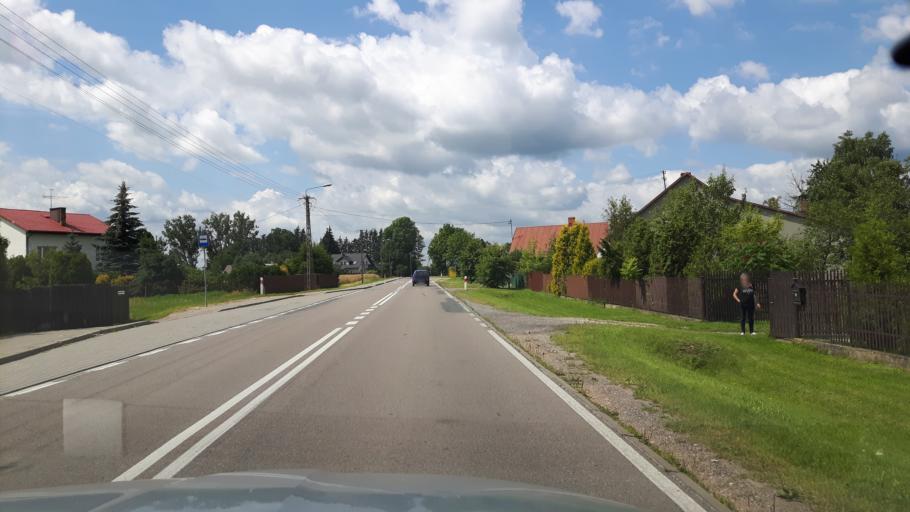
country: PL
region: Masovian Voivodeship
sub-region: Powiat ostrowski
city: Brok
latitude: 52.7028
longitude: 21.8808
